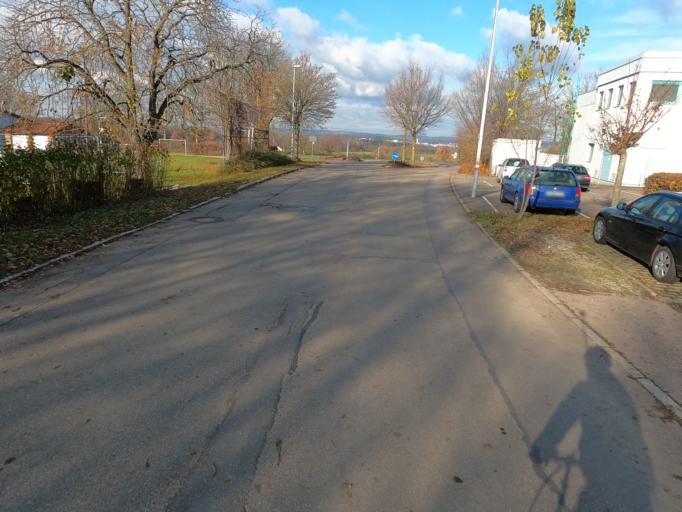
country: DE
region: Baden-Wuerttemberg
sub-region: Regierungsbezirk Stuttgart
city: Hattenhofen
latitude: 48.6653
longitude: 9.5534
